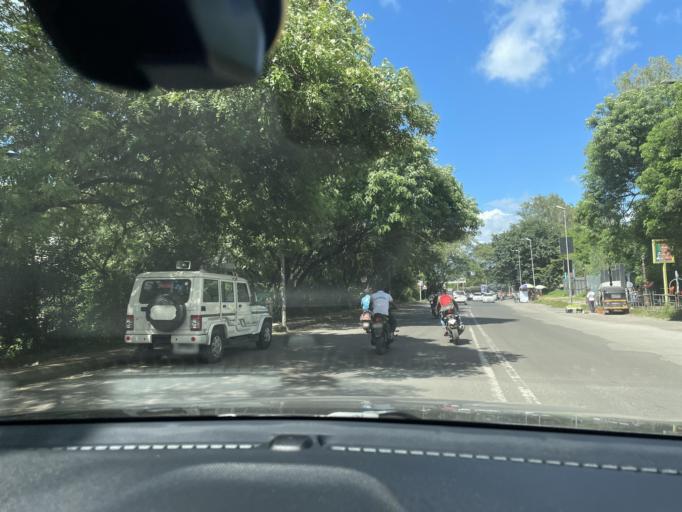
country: IN
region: Maharashtra
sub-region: Pune Division
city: Shivaji Nagar
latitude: 18.5245
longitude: 73.7807
